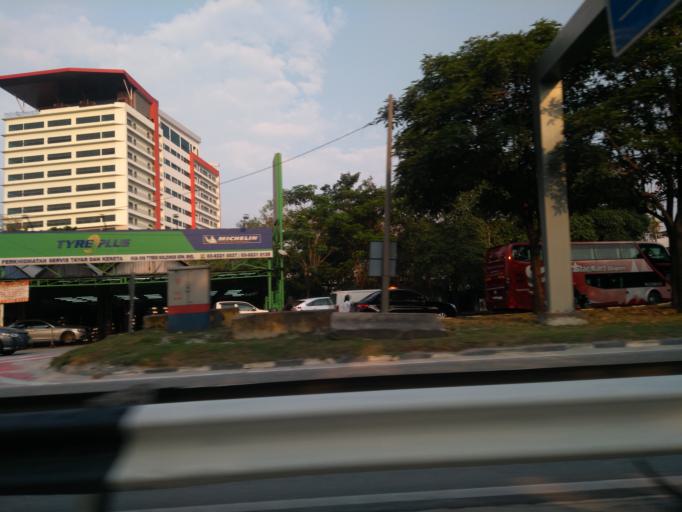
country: MY
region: Kuala Lumpur
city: Kuala Lumpur
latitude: 3.1177
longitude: 101.7082
